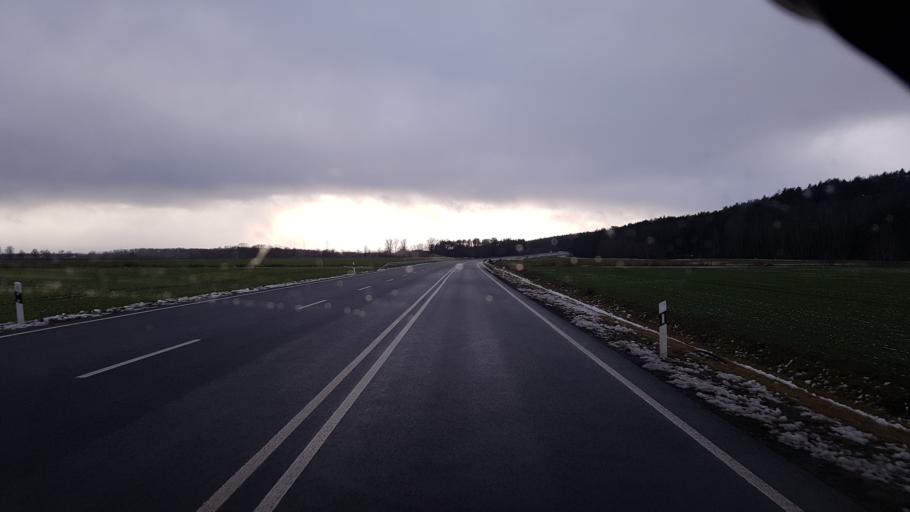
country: DE
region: Brandenburg
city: Schenkendobern
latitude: 51.8640
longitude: 14.6157
